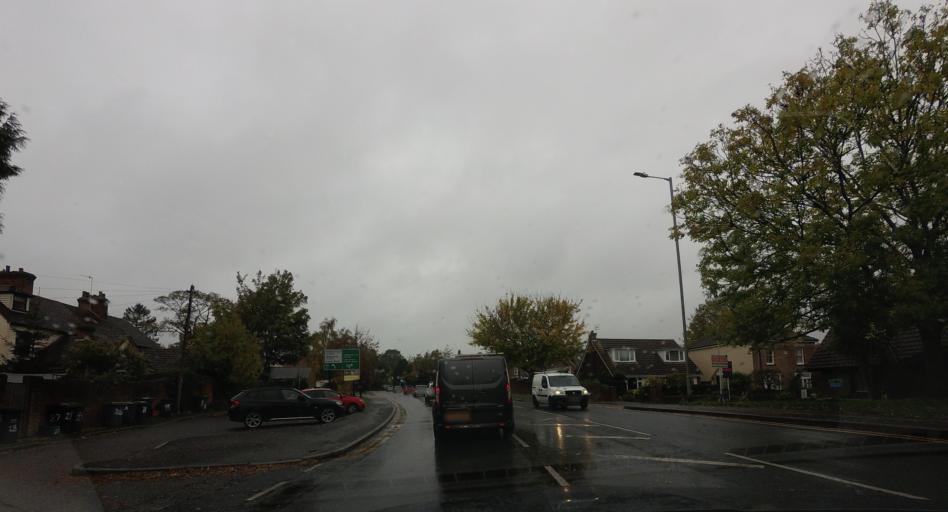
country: GB
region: England
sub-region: Kent
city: Tonbridge
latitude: 51.1992
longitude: 0.2835
